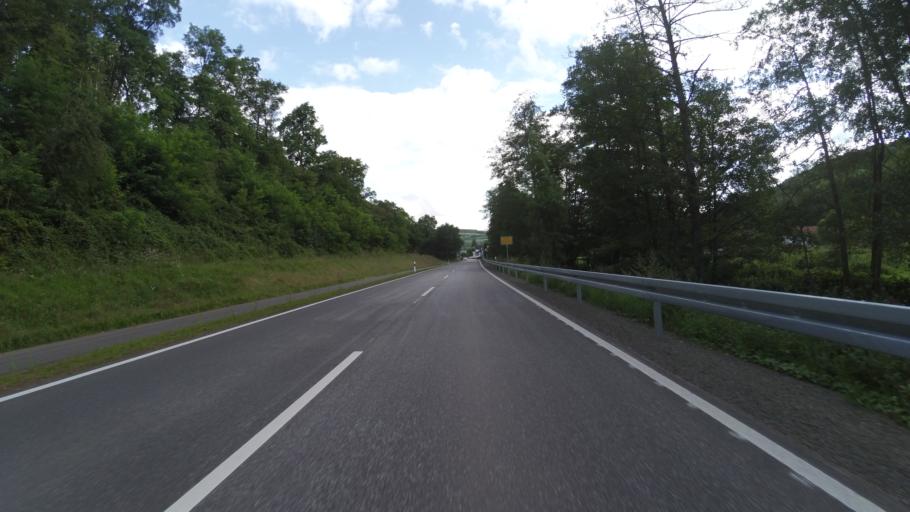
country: DE
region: Saarland
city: Nonnweiler
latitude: 49.5443
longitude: 6.9741
